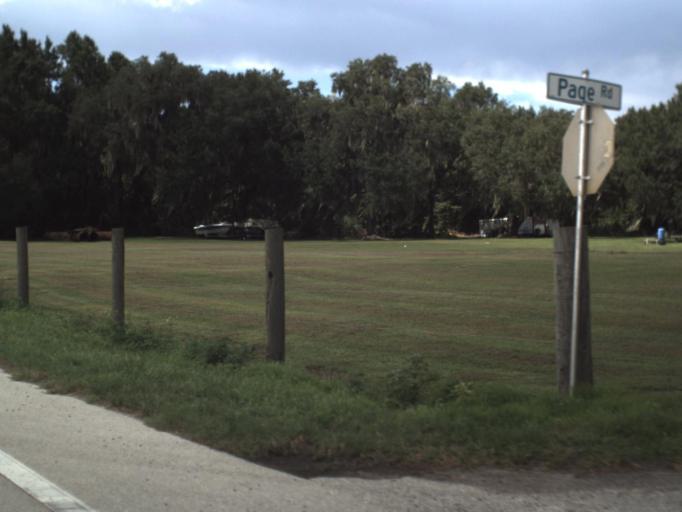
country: US
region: Florida
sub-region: Polk County
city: Fort Meade
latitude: 27.7517
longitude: -81.7709
